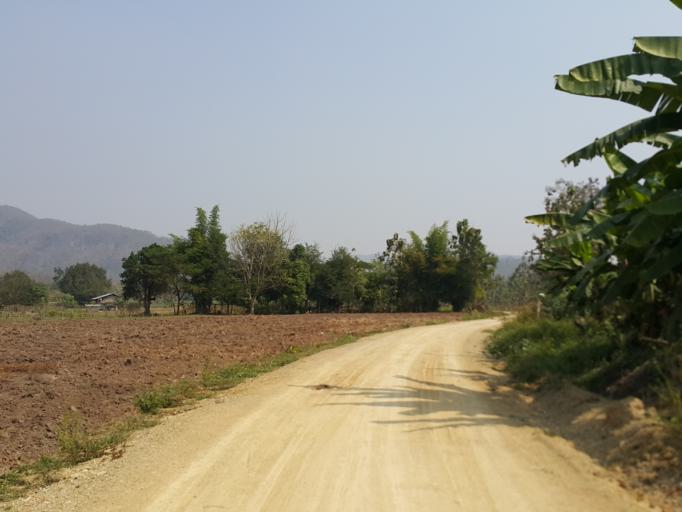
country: TH
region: Sukhothai
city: Thung Saliam
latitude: 17.3369
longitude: 99.4628
